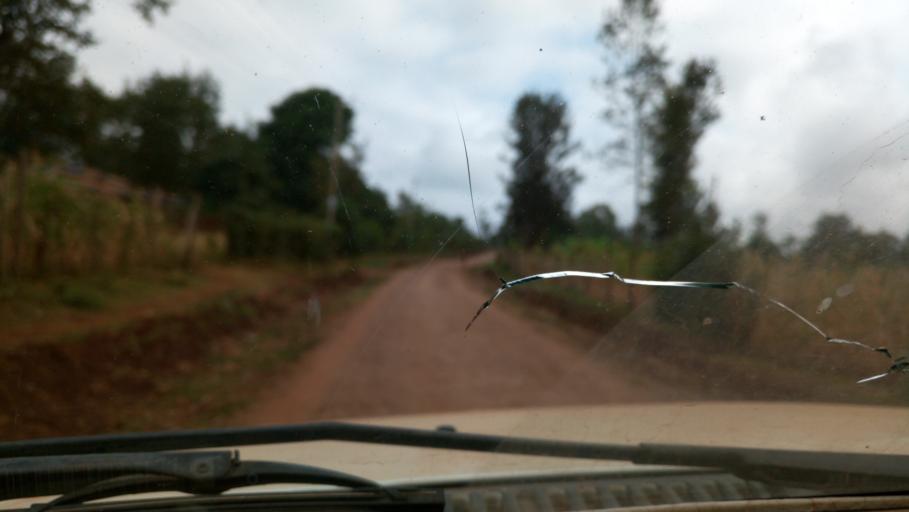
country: KE
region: Murang'a District
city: Maragua
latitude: -0.8523
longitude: 37.1020
